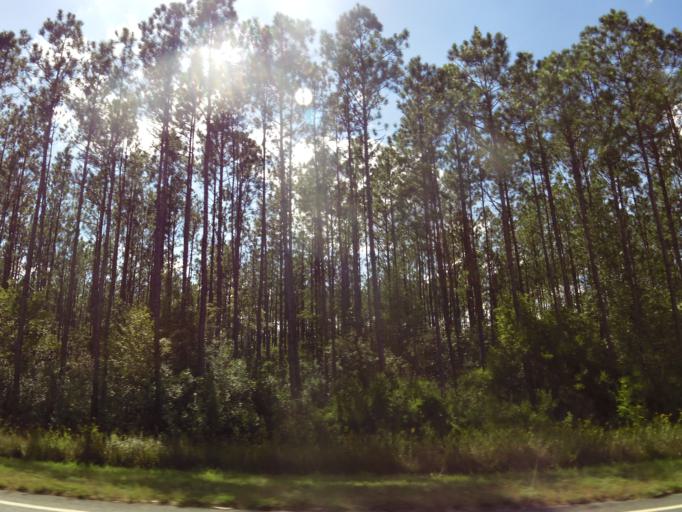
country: US
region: Georgia
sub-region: Clinch County
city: Homerville
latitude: 30.7313
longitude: -82.5875
